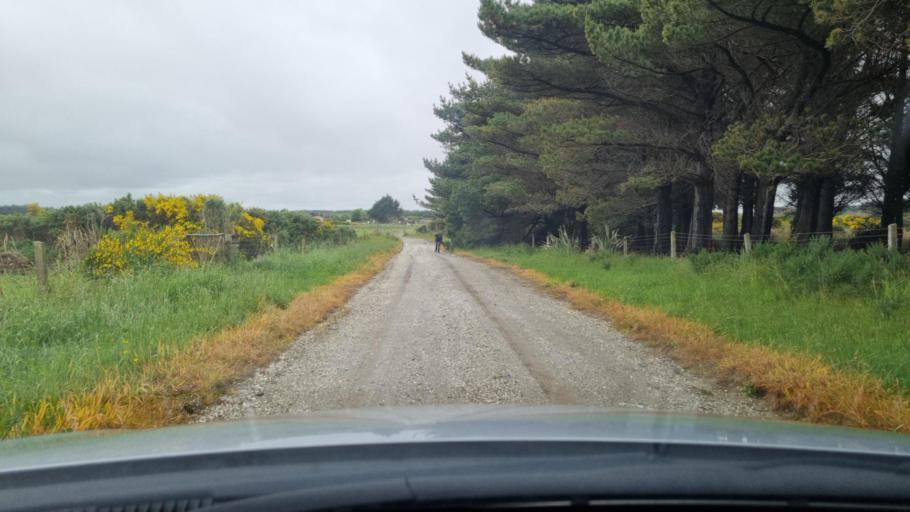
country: NZ
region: Southland
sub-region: Invercargill City
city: Invercargill
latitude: -46.4669
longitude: 168.3817
